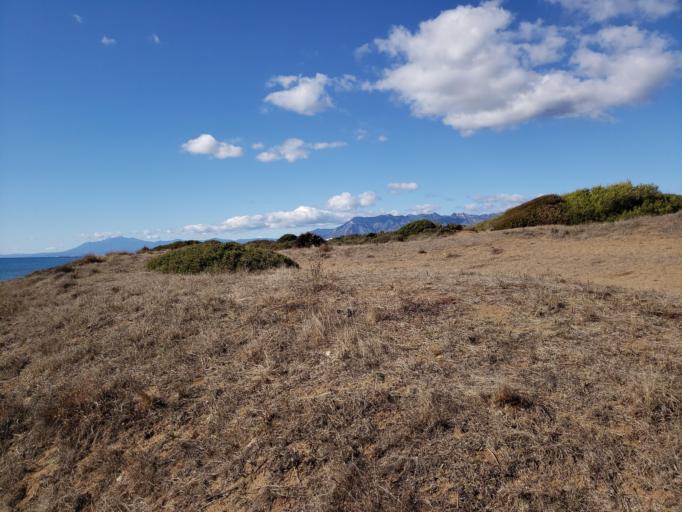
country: ES
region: Andalusia
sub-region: Provincia de Malaga
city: Fuengirola
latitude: 36.4850
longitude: -4.7437
